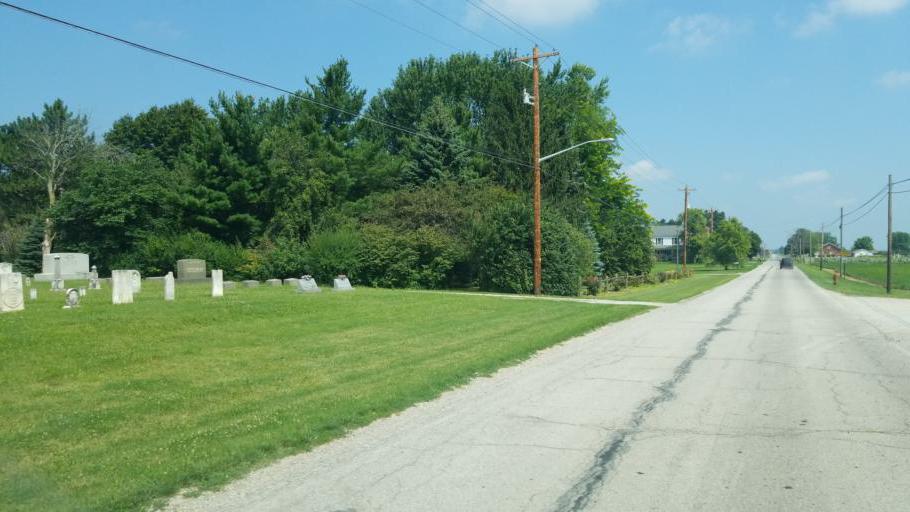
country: US
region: Ohio
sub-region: Huron County
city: Willard
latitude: 40.9650
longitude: -82.8536
